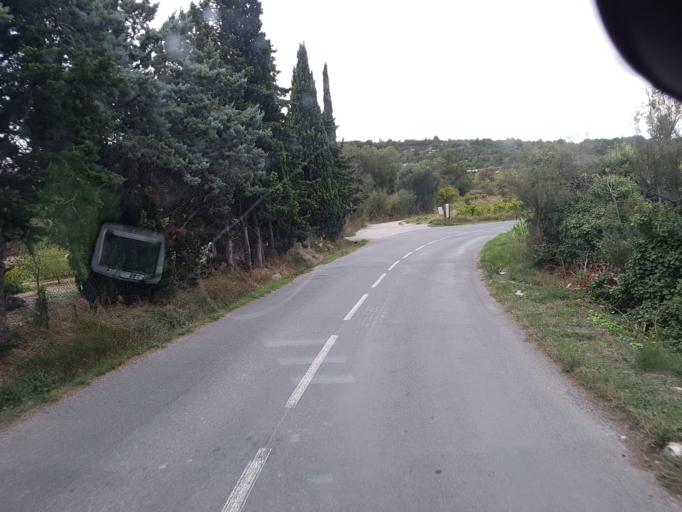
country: FR
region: Languedoc-Roussillon
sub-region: Departement de l'Aude
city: Peyriac-de-Mer
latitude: 43.1238
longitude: 2.9885
